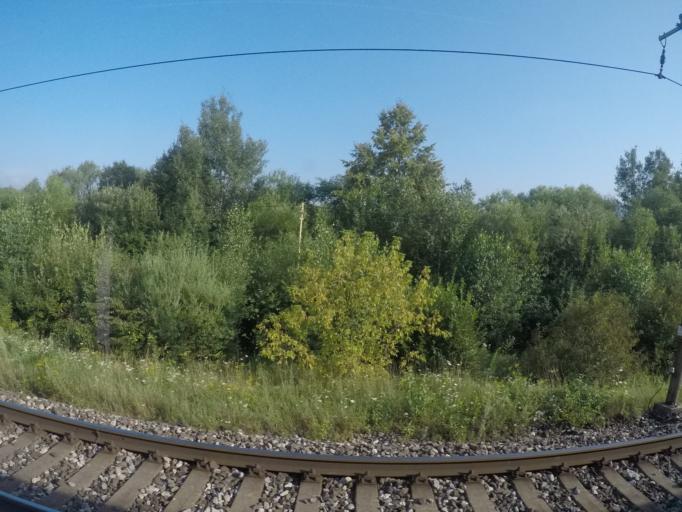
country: SK
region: Kosicky
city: Gelnica
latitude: 48.9131
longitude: 20.9445
